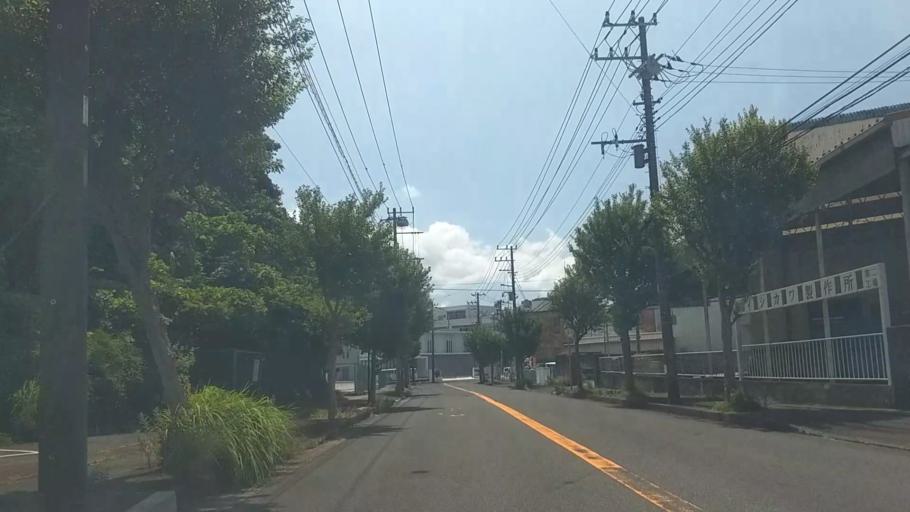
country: JP
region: Kanagawa
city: Yokosuka
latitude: 35.3131
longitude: 139.6413
